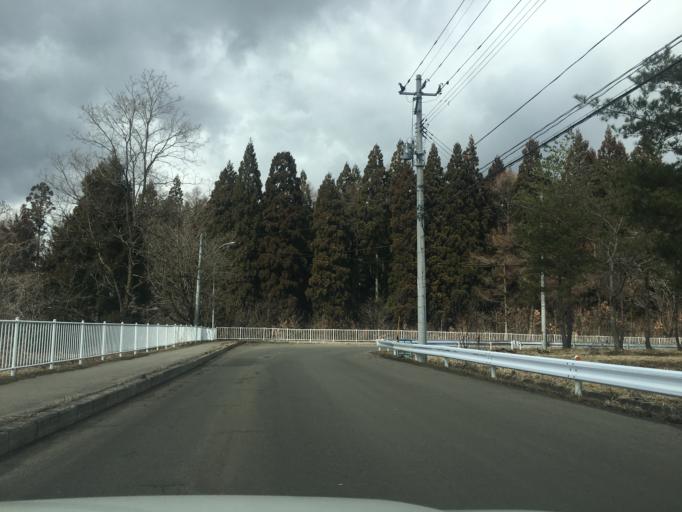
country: JP
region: Akita
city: Takanosu
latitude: 40.1856
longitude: 140.3396
